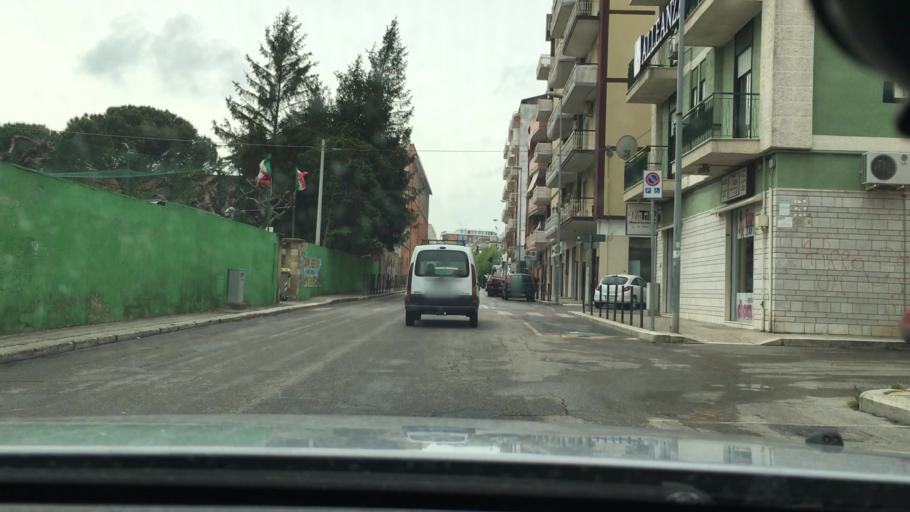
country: IT
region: Apulia
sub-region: Provincia di Bari
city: Gioia del Colle
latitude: 40.8051
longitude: 16.9238
